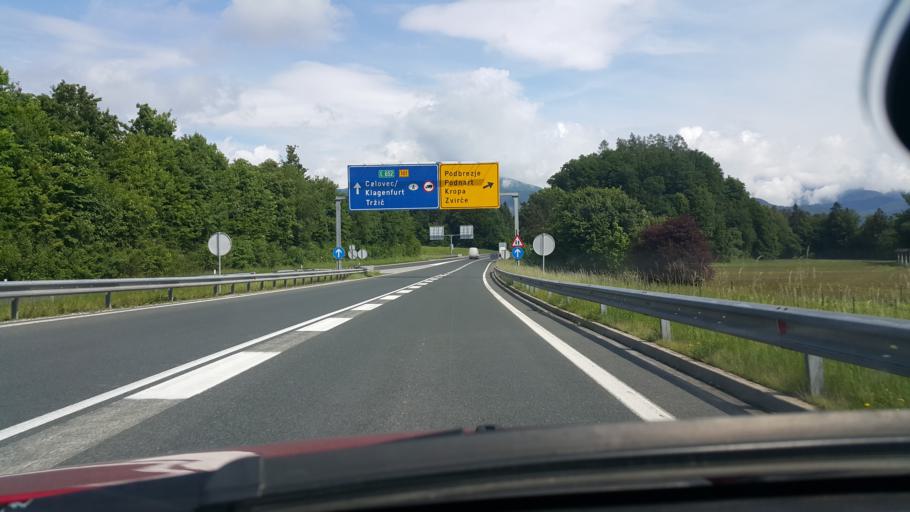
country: SI
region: Trzic
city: Bistrica pri Trzicu
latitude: 46.3105
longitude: 14.2793
